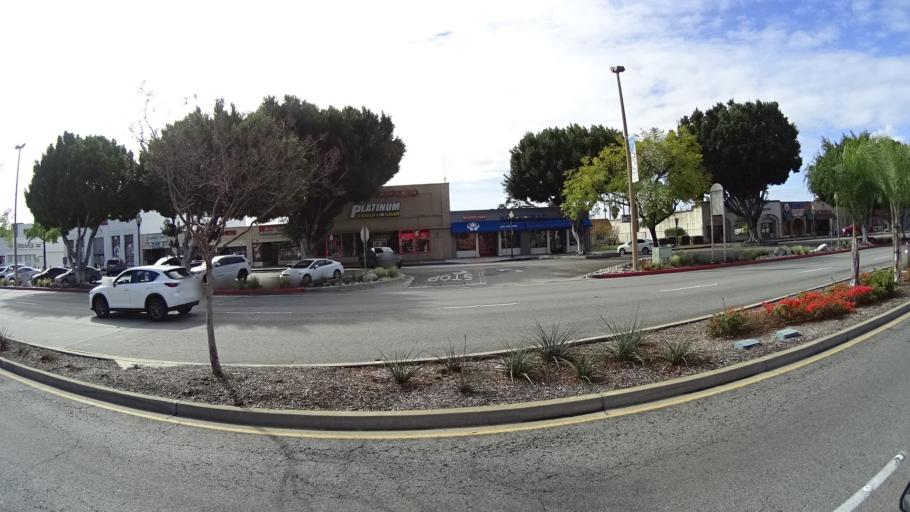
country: US
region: California
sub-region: Los Angeles County
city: Baldwin Park
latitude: 34.0865
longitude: -117.9611
